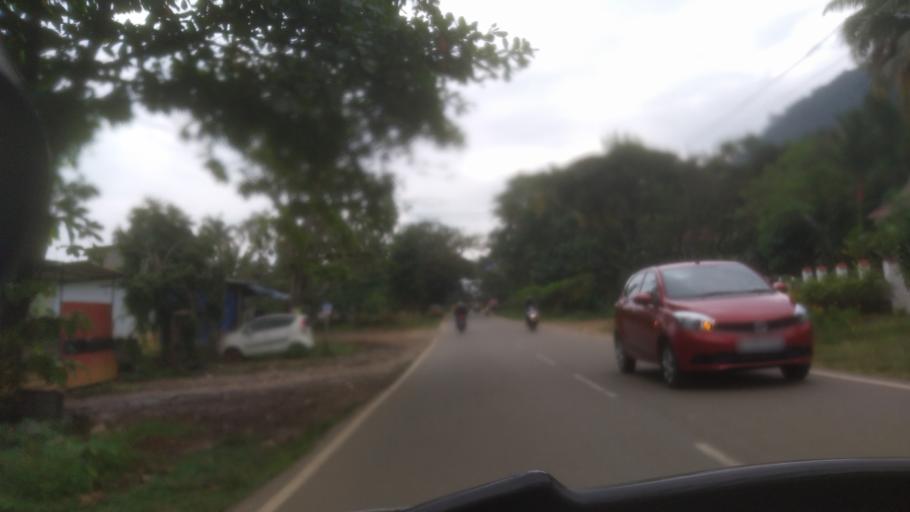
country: IN
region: Kerala
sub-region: Idukki
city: Munnar
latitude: 9.9977
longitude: 76.9732
